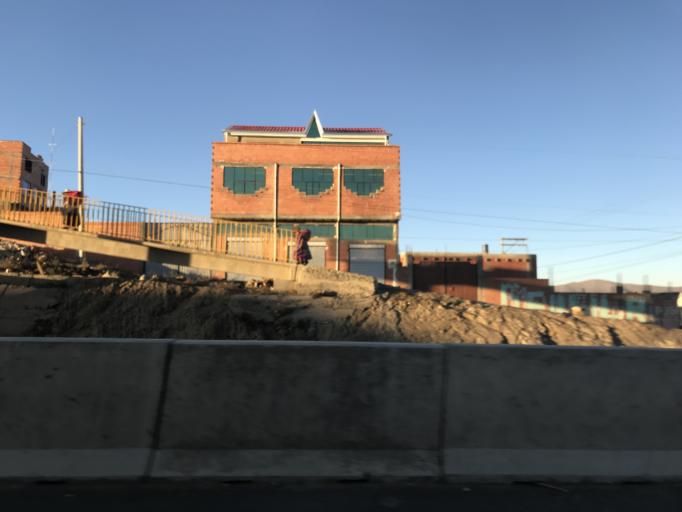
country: BO
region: La Paz
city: Batallas
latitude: -16.2981
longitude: -68.5284
